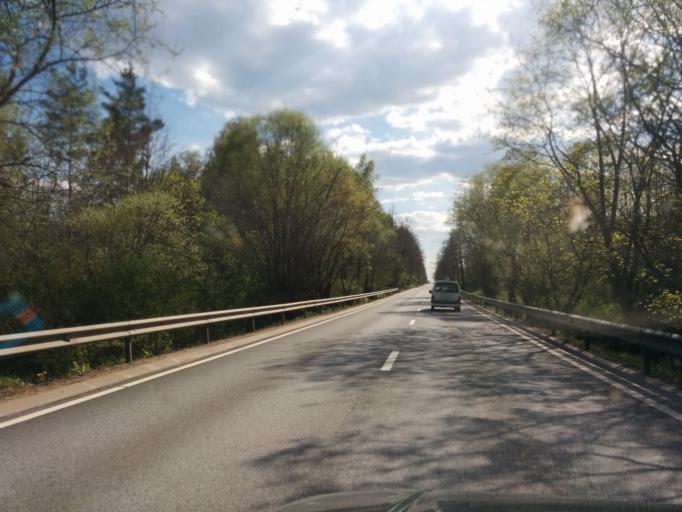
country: LV
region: Seja
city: Loja
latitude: 57.1501
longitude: 24.6821
